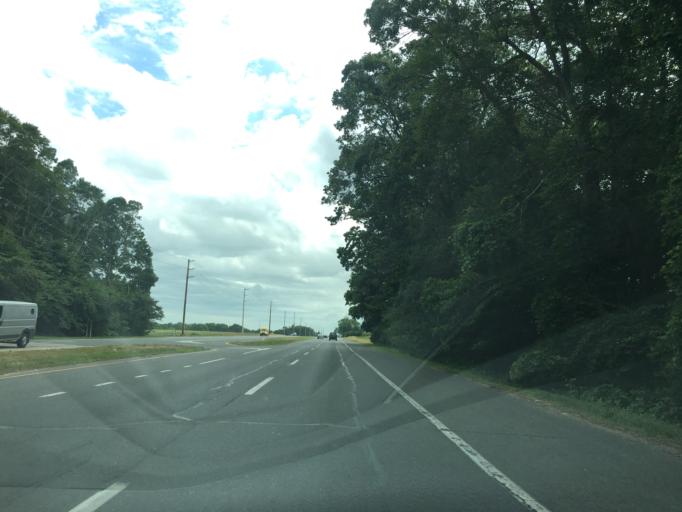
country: US
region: New York
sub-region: Suffolk County
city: Cutchogue
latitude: 41.0151
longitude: -72.5118
